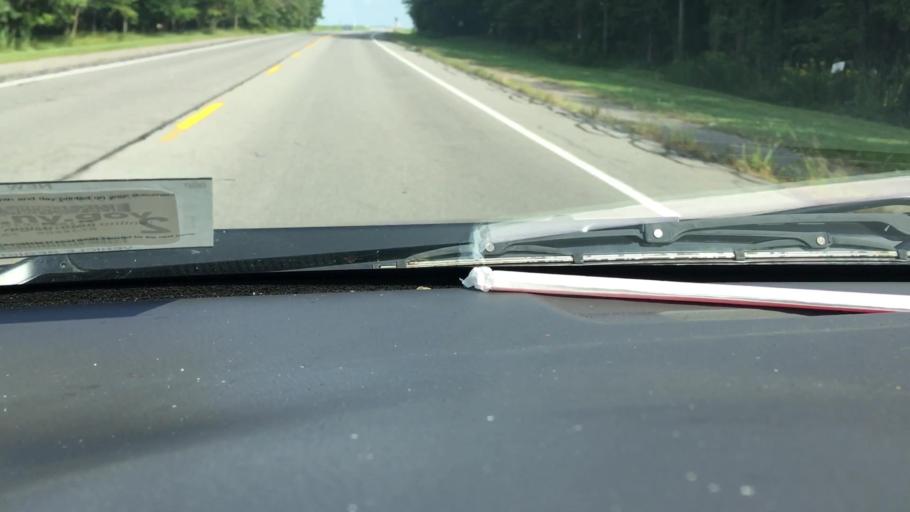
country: US
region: New York
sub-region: Genesee County
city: Batavia
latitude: 43.0147
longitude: -78.1492
